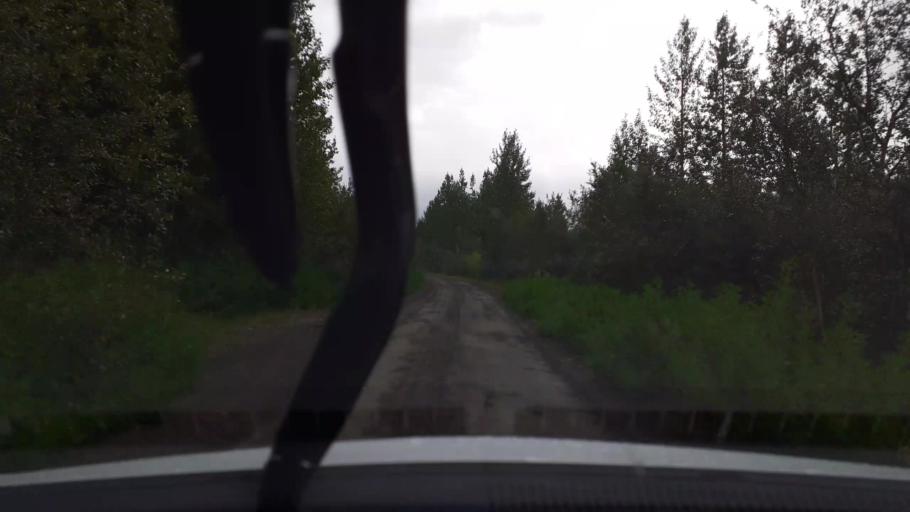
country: IS
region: Capital Region
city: Mosfellsbaer
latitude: 64.4959
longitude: -21.3546
